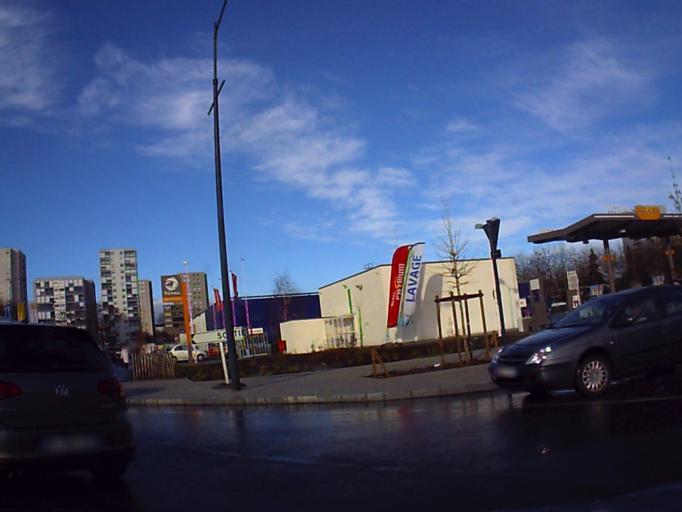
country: FR
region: Brittany
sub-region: Departement d'Ille-et-Vilaine
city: Rennes
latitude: 48.0838
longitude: -1.6768
